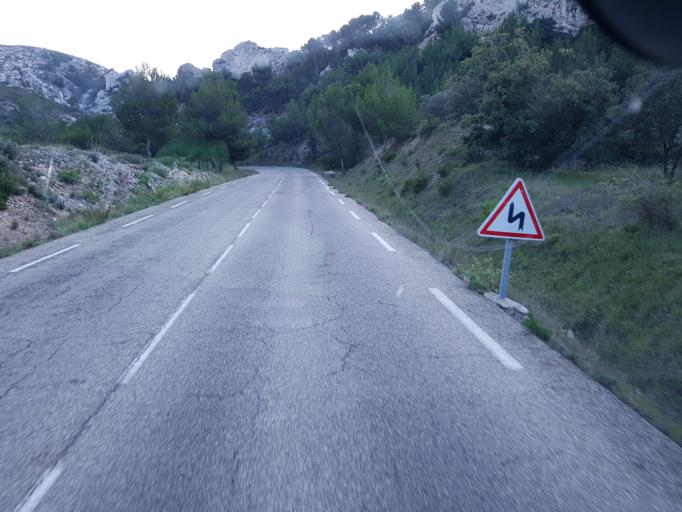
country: FR
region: Provence-Alpes-Cote d'Azur
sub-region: Departement des Bouches-du-Rhone
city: Le Rove
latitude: 43.3535
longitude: 5.2352
